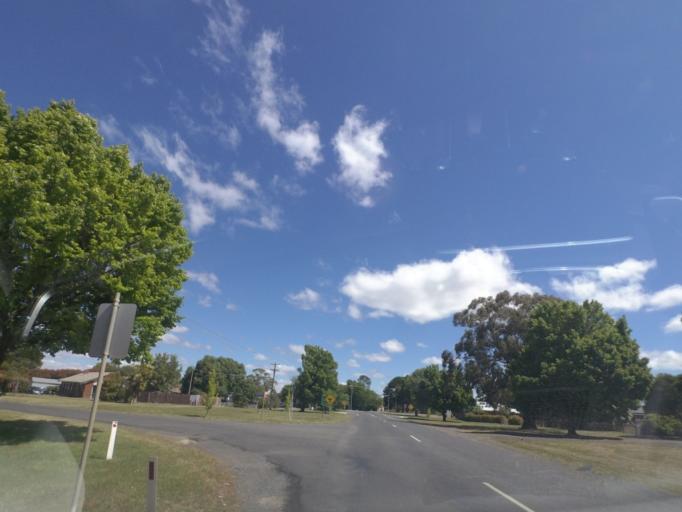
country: AU
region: Victoria
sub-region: Mount Alexander
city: Castlemaine
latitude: -37.3244
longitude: 144.4068
